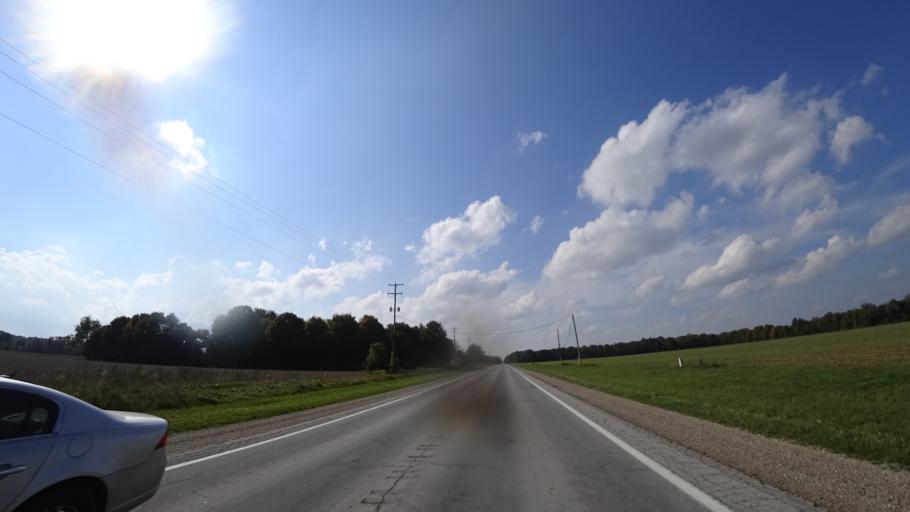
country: US
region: Michigan
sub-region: Saint Joseph County
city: Colon
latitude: 42.0102
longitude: -85.3751
